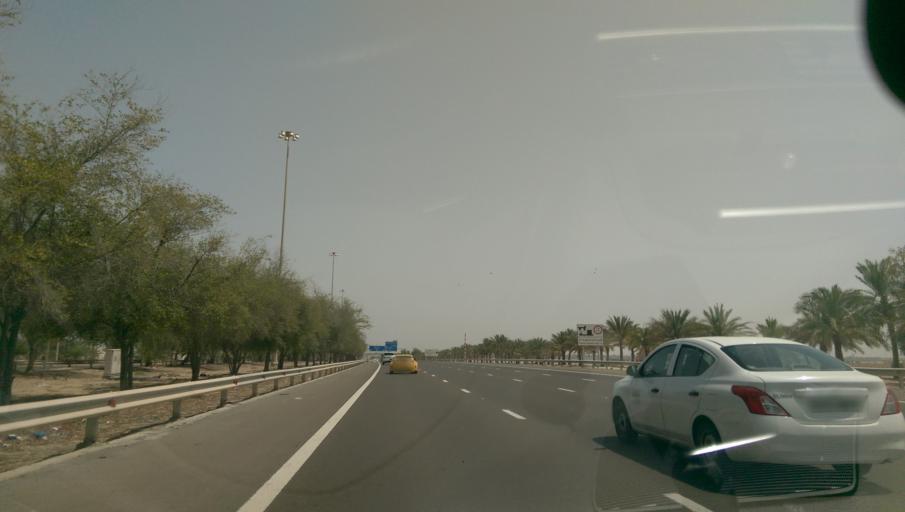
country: AE
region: Abu Dhabi
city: Abu Dhabi
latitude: 24.4519
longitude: 54.6789
